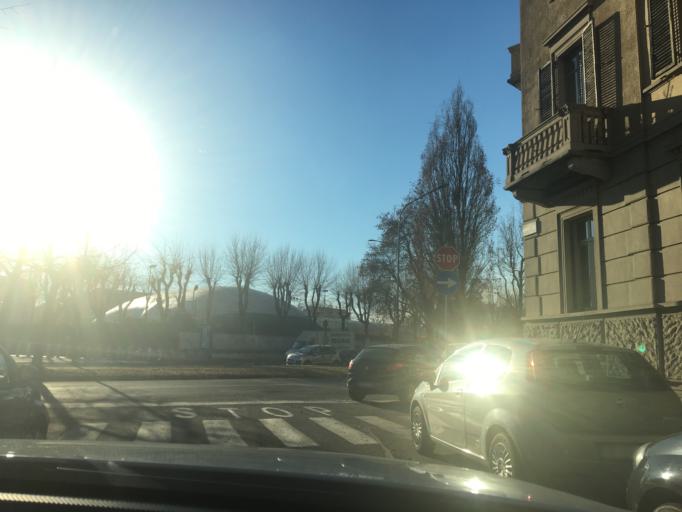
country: IT
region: Piedmont
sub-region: Provincia di Torino
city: Lesna
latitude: 45.0551
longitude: 7.6485
